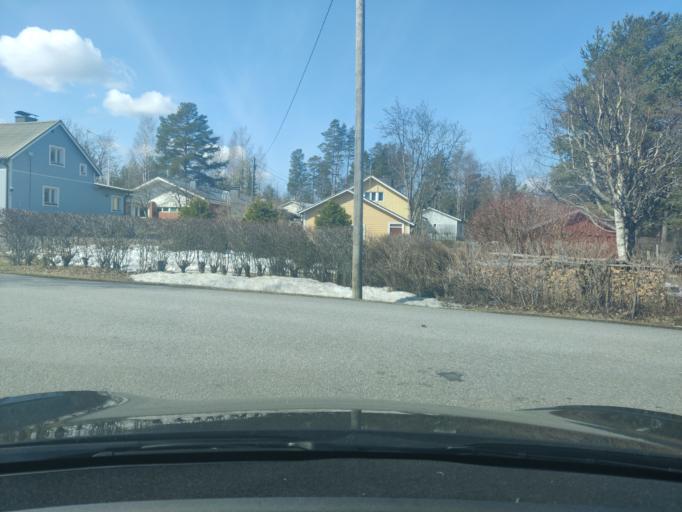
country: FI
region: Northern Savo
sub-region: Kuopio
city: Vehmersalmi
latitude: 62.9128
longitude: 28.1622
